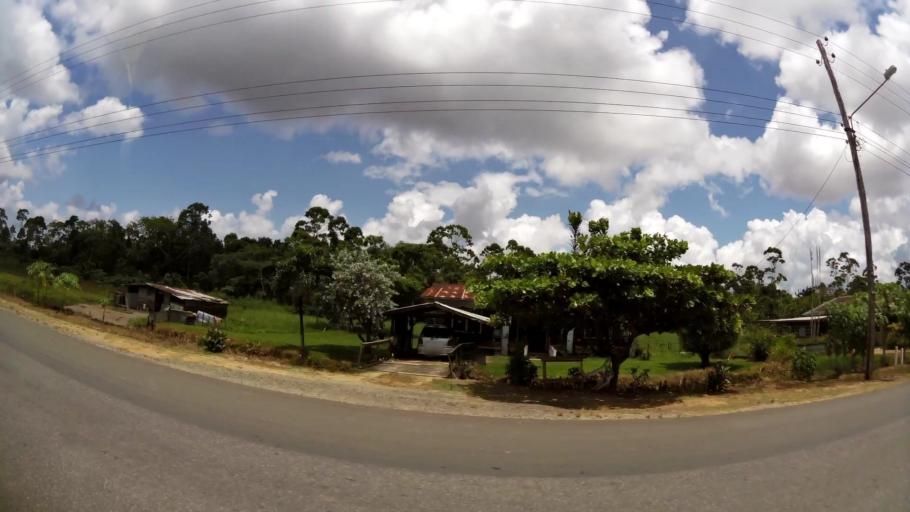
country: SR
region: Paramaribo
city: Paramaribo
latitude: 5.8031
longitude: -55.1244
